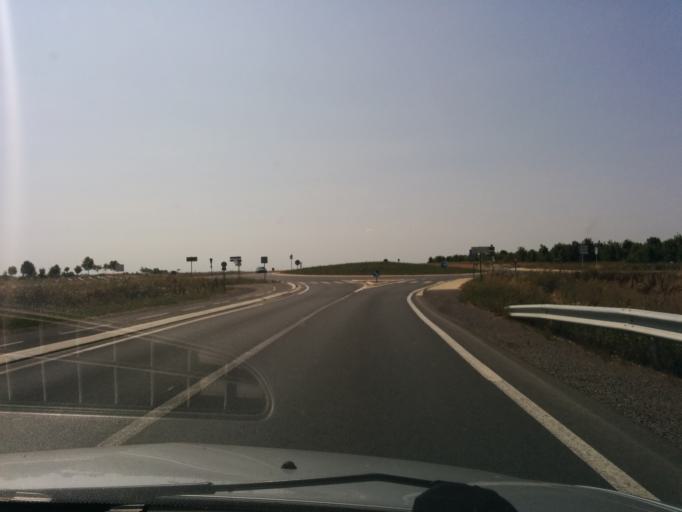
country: FR
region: Poitou-Charentes
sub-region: Departement de la Vienne
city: Jaunay-Clan
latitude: 46.6841
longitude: 0.3578
